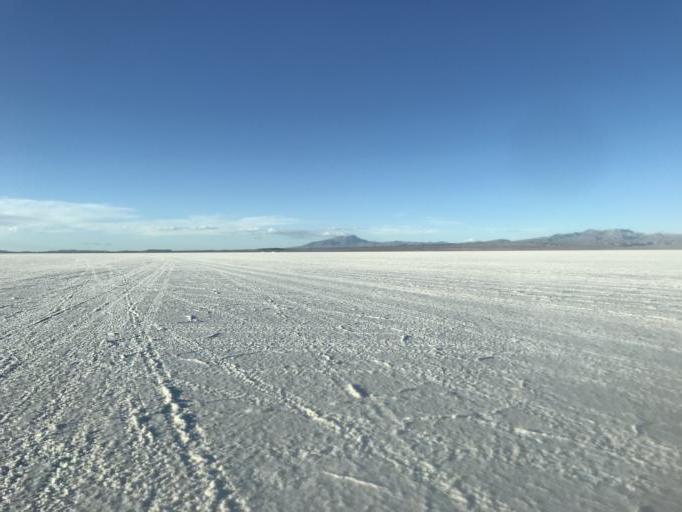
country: BO
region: Potosi
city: Colchani
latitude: -20.3670
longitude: -67.0072
